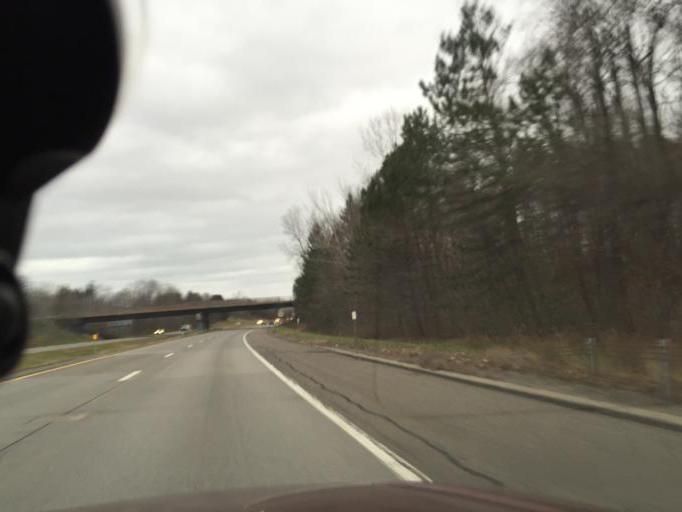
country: US
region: New York
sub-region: Monroe County
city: Greece
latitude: 43.2369
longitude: -77.6714
